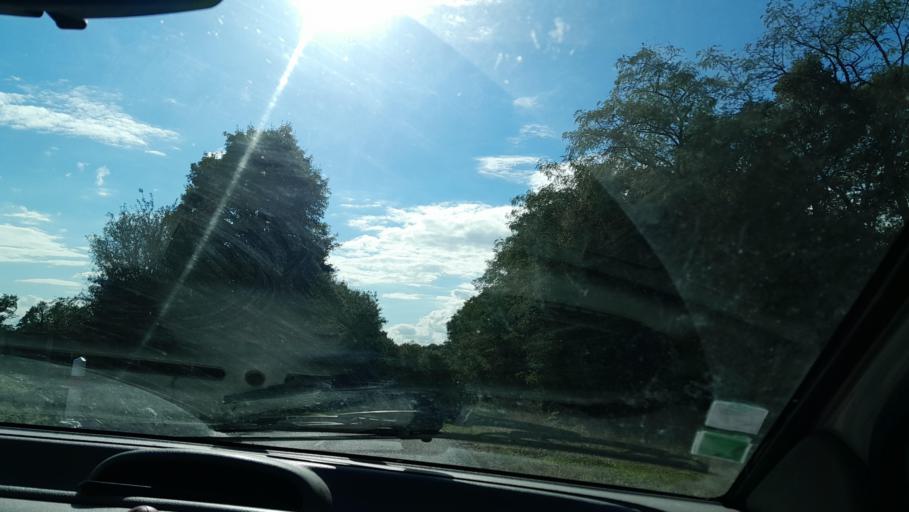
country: FR
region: Pays de la Loire
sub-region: Departement de la Mayenne
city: Ahuille
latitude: 48.0271
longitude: -0.8554
